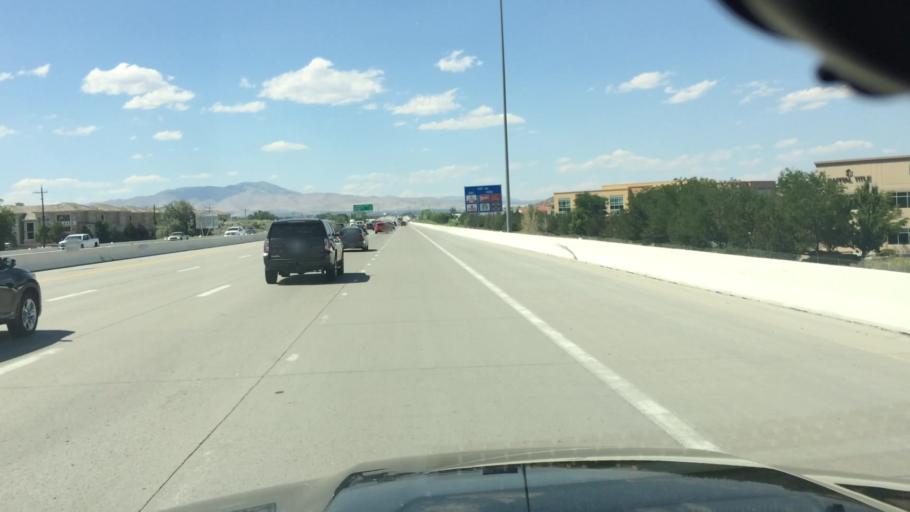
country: US
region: Nevada
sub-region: Washoe County
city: Sparks
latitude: 39.4282
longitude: -119.7570
